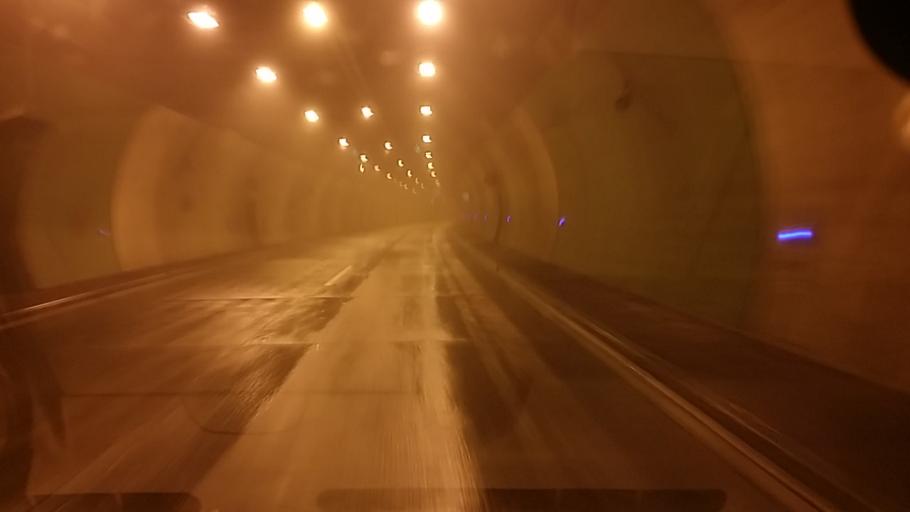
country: CZ
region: Ustecky
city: Libouchec
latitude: 50.7634
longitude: 13.9714
